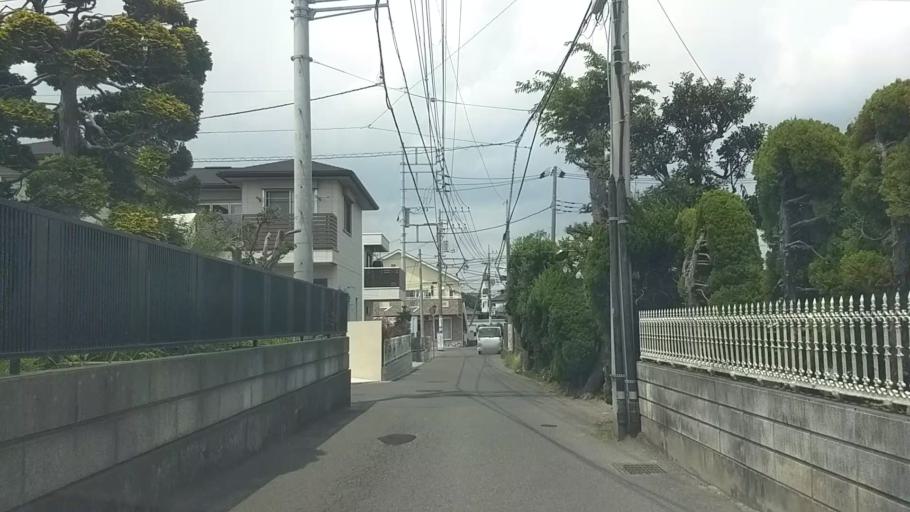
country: JP
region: Kanagawa
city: Chigasaki
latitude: 35.3549
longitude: 139.3979
